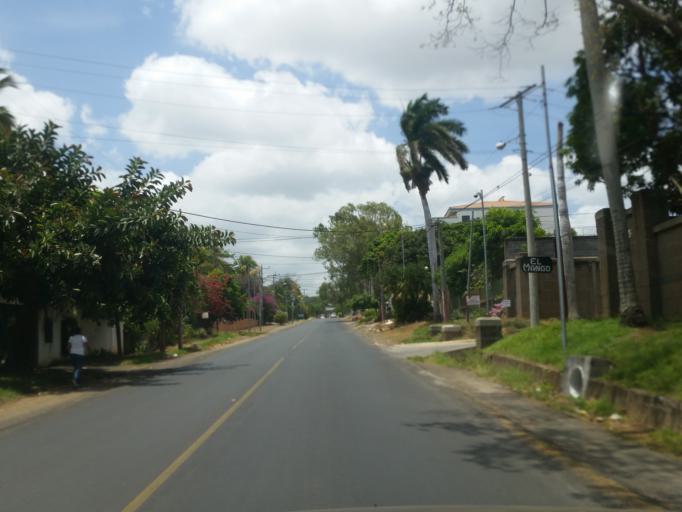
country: NI
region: Managua
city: Managua
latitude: 12.0897
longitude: -86.2399
